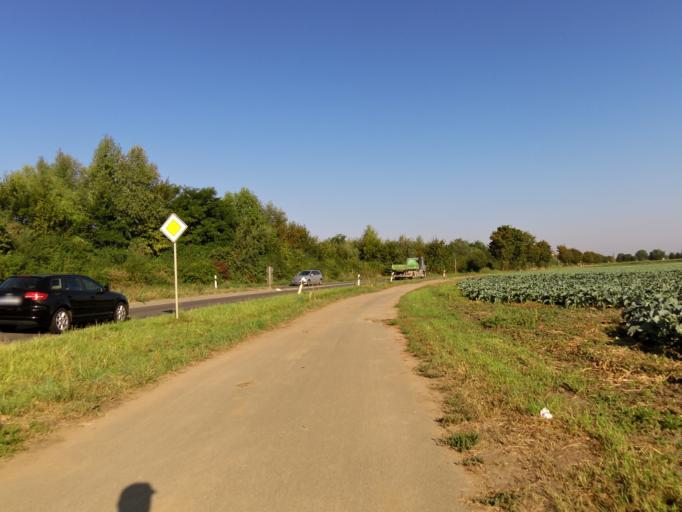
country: DE
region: Rheinland-Pfalz
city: Maxdorf
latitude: 49.4884
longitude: 8.2958
